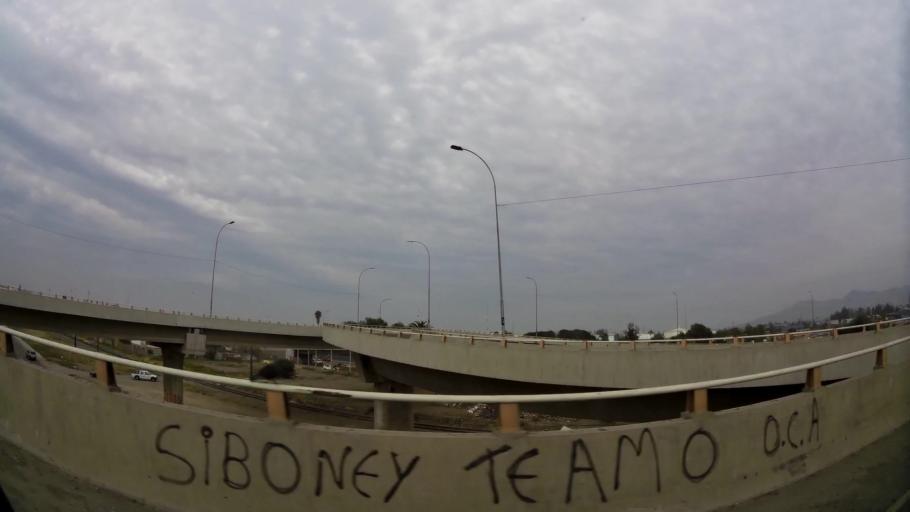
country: CL
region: Santiago Metropolitan
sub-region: Provincia de Santiago
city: Lo Prado
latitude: -33.5253
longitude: -70.7554
